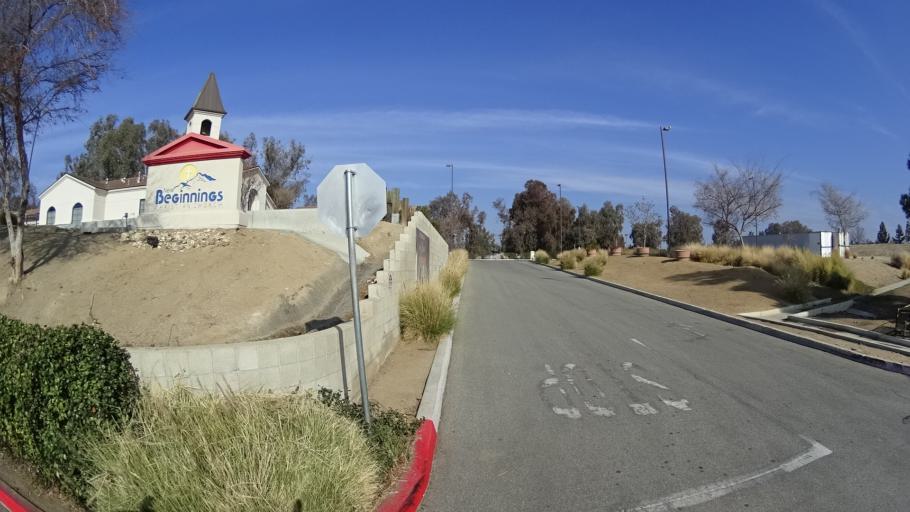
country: US
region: California
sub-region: Kern County
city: Bakersfield
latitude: 35.3938
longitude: -118.9653
